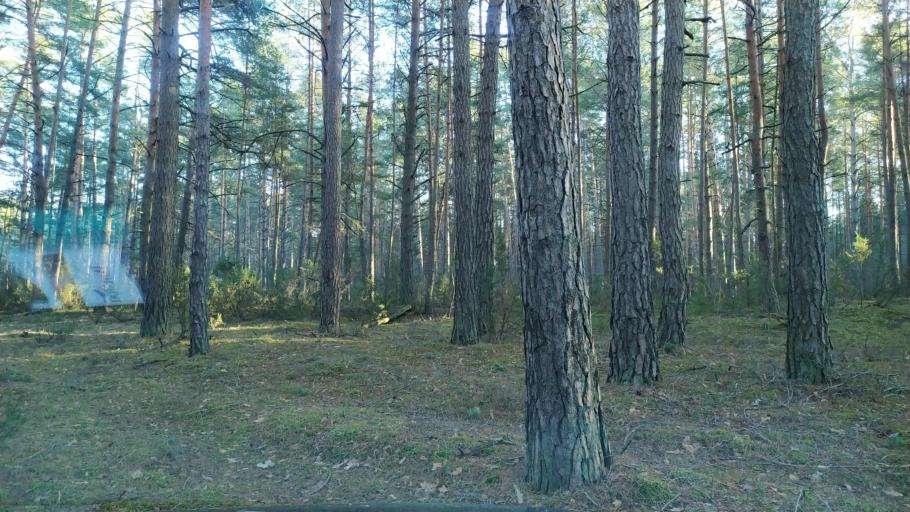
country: BY
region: Brest
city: Pruzhany
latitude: 52.5507
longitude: 24.2803
